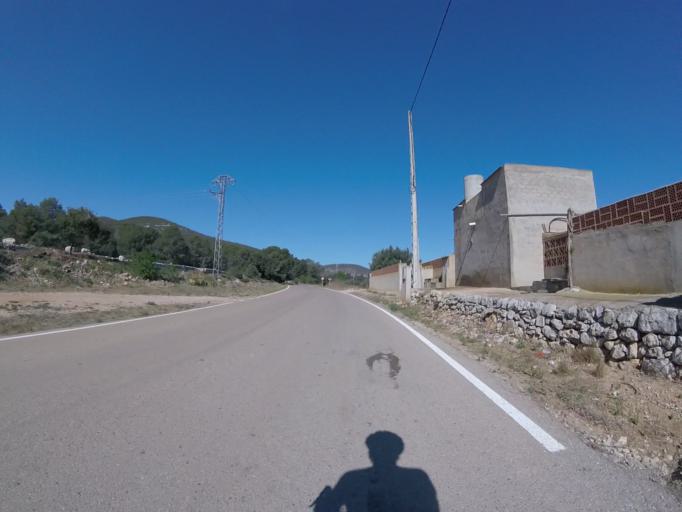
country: ES
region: Valencia
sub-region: Provincia de Castello
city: Santa Magdalena de Pulpis
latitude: 40.3640
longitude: 0.2793
